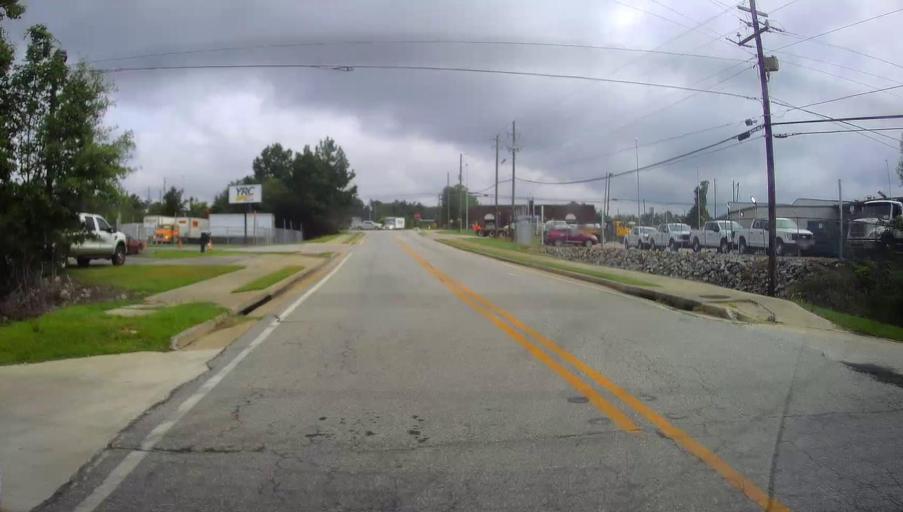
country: US
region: Georgia
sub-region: Bibb County
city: West Point
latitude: 32.8311
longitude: -83.7292
